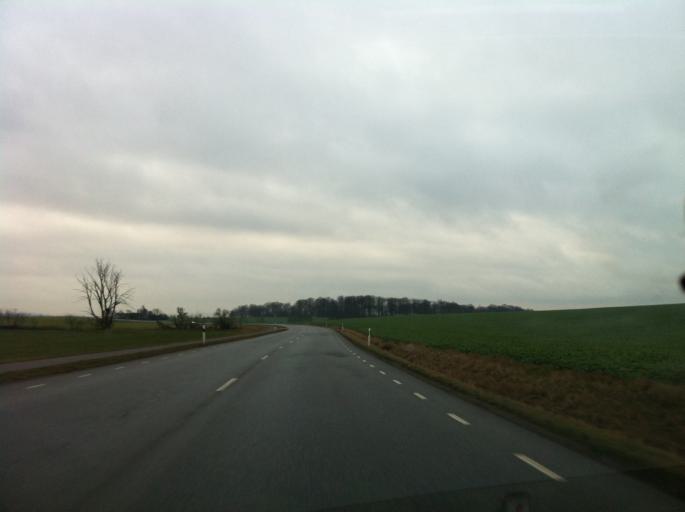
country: SE
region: Skane
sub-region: Helsingborg
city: Glumslov
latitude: 55.9280
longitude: 12.8184
